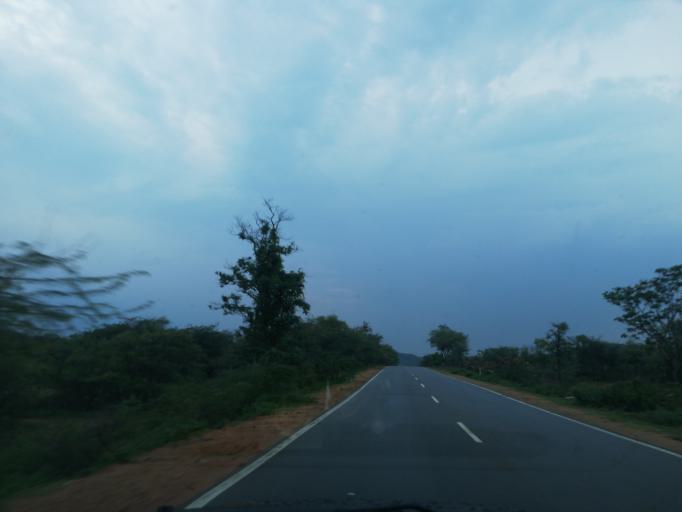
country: IN
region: Andhra Pradesh
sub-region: Guntur
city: Macherla
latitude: 16.6491
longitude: 79.2896
